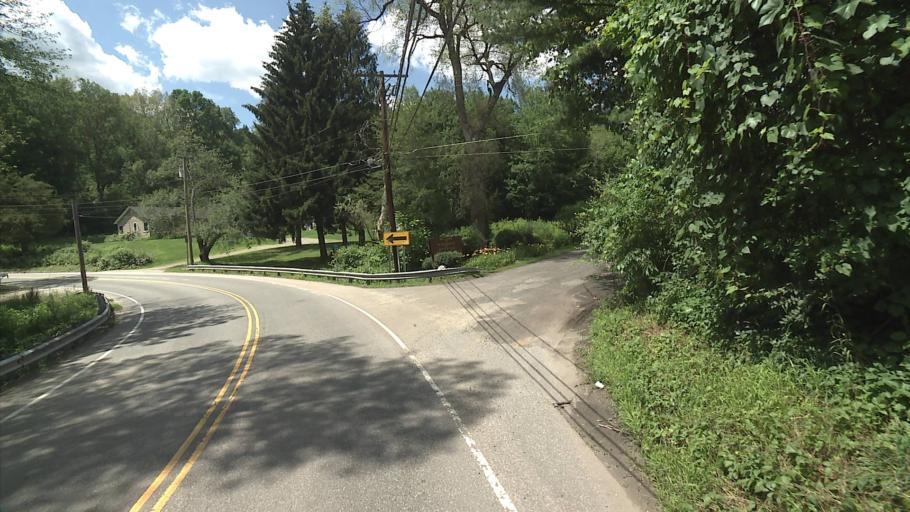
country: US
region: Connecticut
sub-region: Windham County
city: Quinebaug
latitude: 42.0177
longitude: -71.9618
